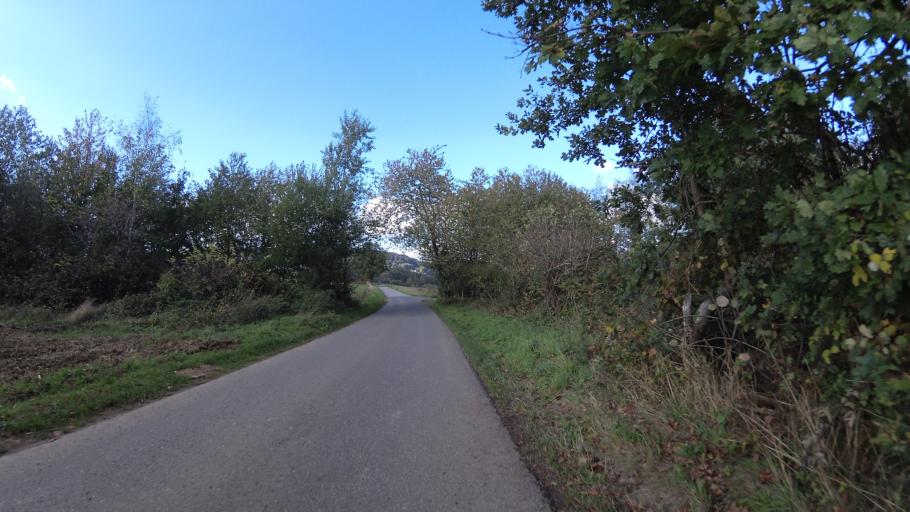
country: DE
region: Saarland
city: Tholey
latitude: 49.4680
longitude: 7.0454
